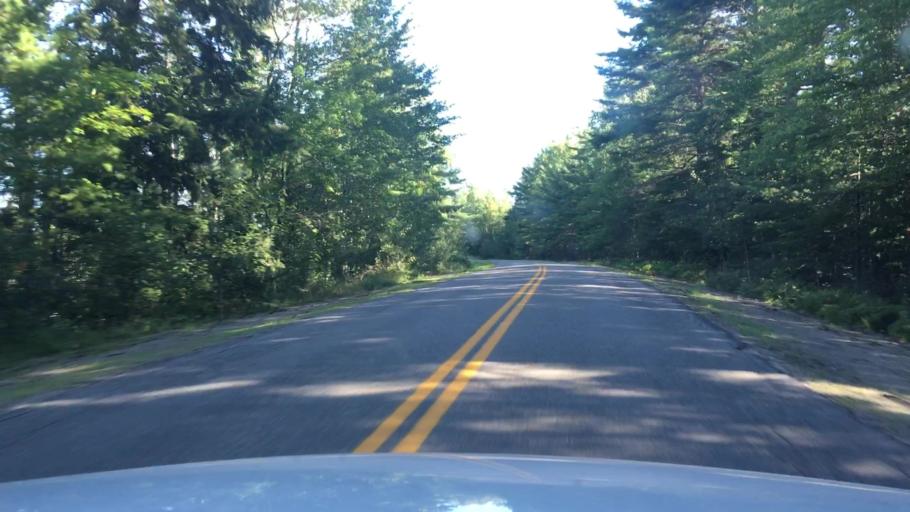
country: US
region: Maine
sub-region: Penobscot County
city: Enfield
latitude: 45.2322
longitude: -68.5806
